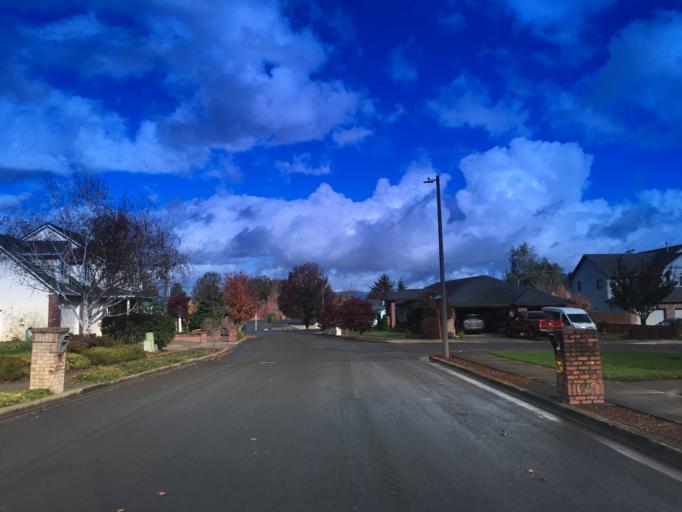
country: US
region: Oregon
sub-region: Multnomah County
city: Troutdale
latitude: 45.5094
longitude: -122.3807
